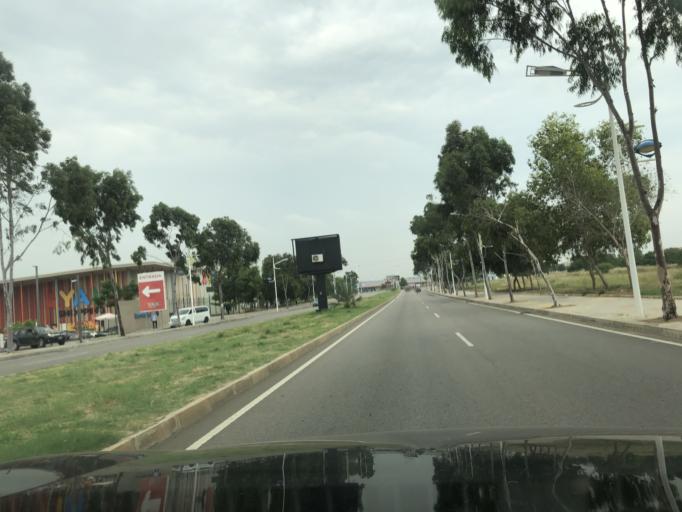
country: AO
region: Luanda
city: Luanda
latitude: -8.9911
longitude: 13.2880
